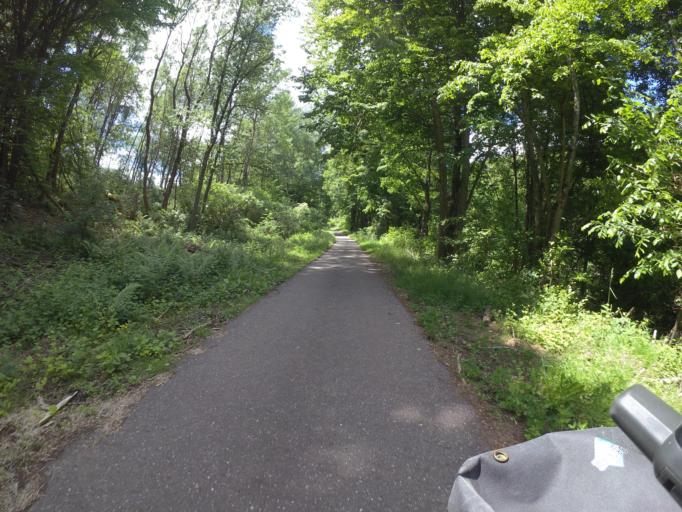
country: DE
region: Rheinland-Pfalz
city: Rumbach
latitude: 49.0849
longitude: 7.7873
